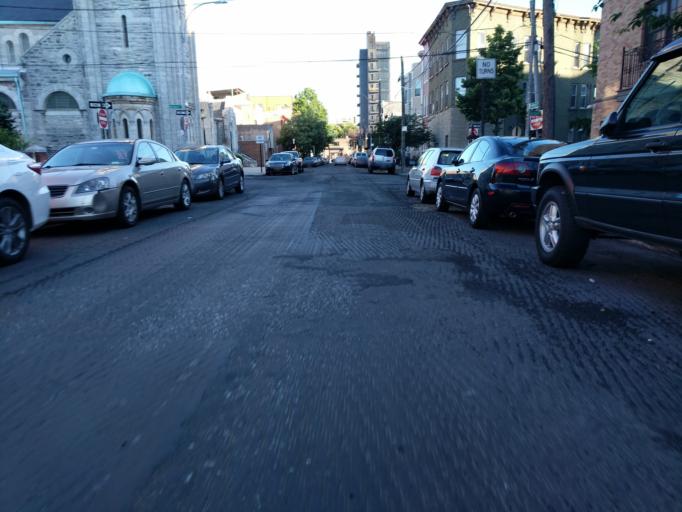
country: US
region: New York
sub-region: Queens County
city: Long Island City
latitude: 40.7205
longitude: -73.9427
